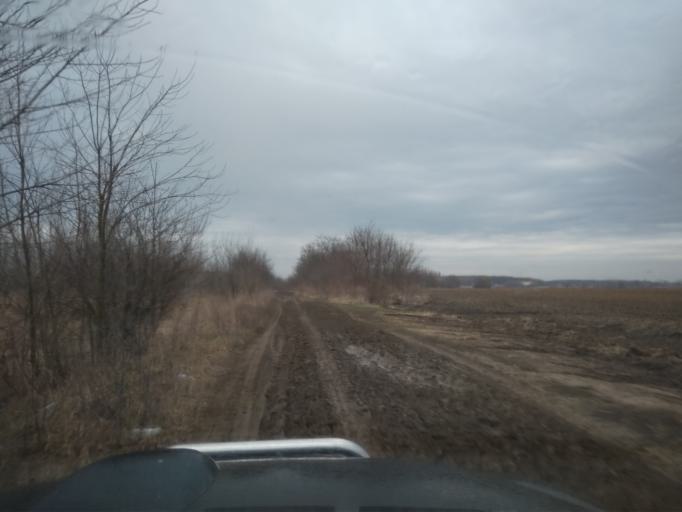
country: HU
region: Szabolcs-Szatmar-Bereg
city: Apagy
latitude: 47.9720
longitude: 21.9197
